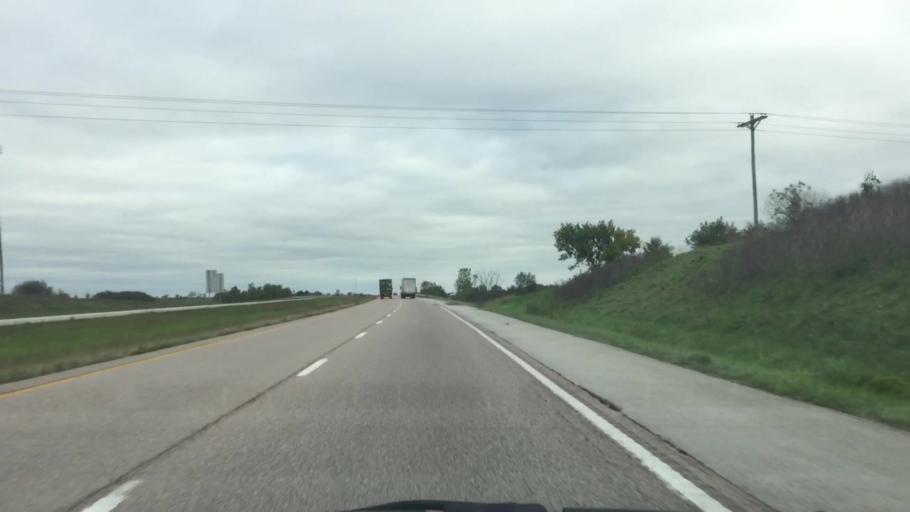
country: US
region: Missouri
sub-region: Clinton County
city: Lathrop
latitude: 39.5714
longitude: -94.2618
